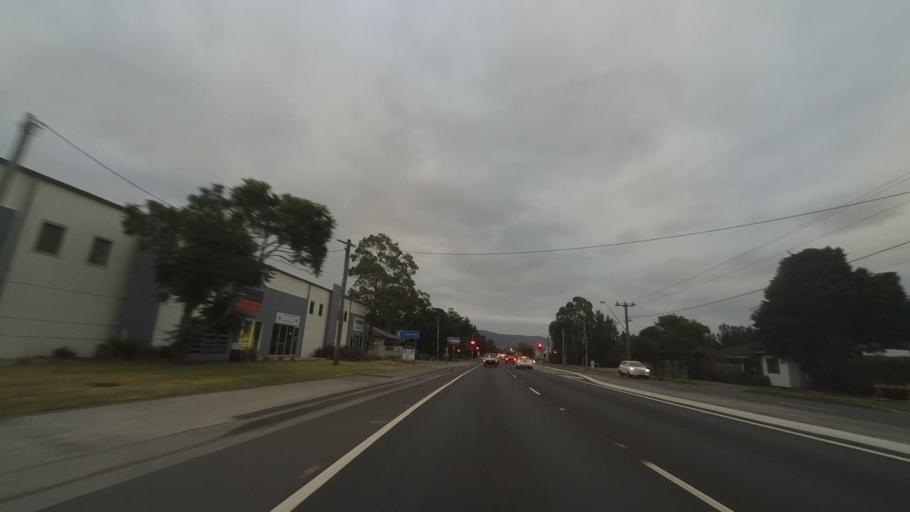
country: AU
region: New South Wales
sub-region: Shellharbour
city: Albion Park Rail
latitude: -34.5573
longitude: 150.7924
